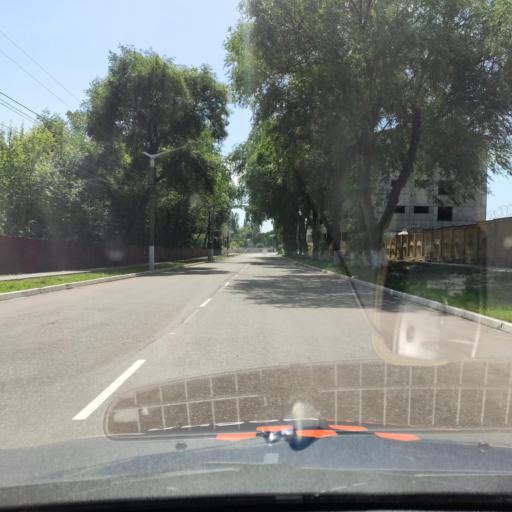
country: RU
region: Voronezj
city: Semiluki
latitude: 51.6905
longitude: 39.0367
